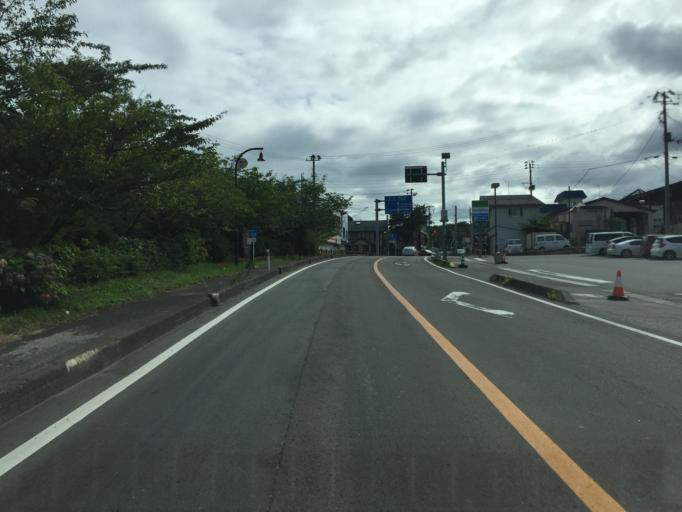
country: JP
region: Fukushima
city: Nihommatsu
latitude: 37.6065
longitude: 140.3580
